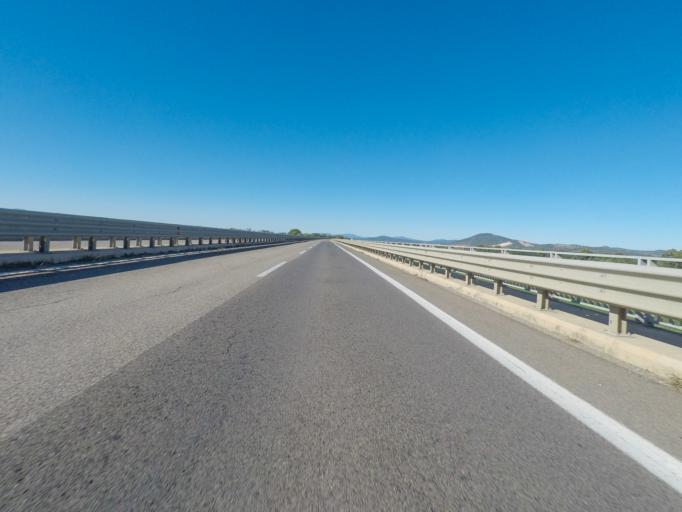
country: IT
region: Tuscany
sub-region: Provincia di Grosseto
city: Grosseto
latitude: 42.7544
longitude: 11.1432
